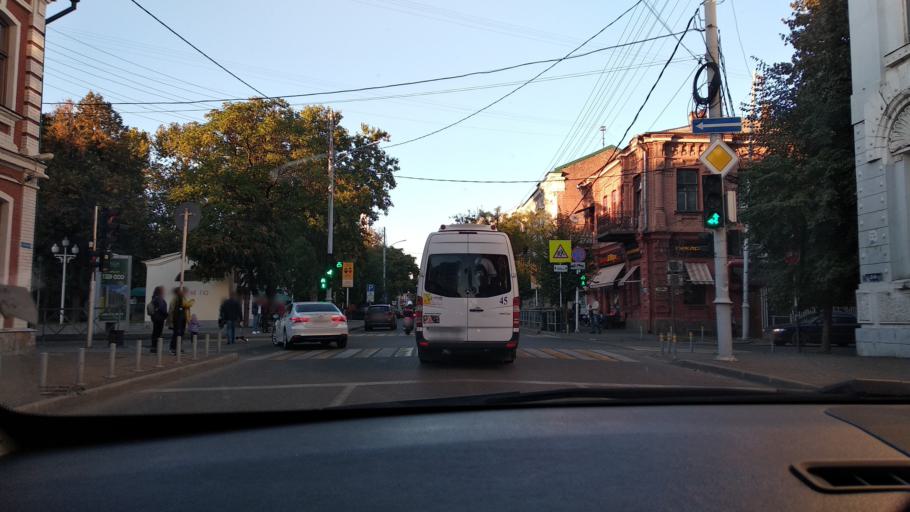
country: RU
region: Krasnodarskiy
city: Krasnodar
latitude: 45.0233
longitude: 38.9721
